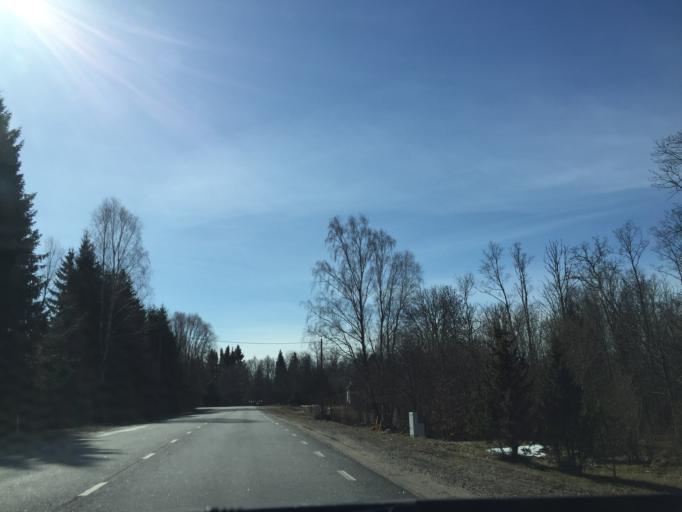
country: EE
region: Laeaene
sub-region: Lihula vald
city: Lihula
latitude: 58.6171
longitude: 23.6914
